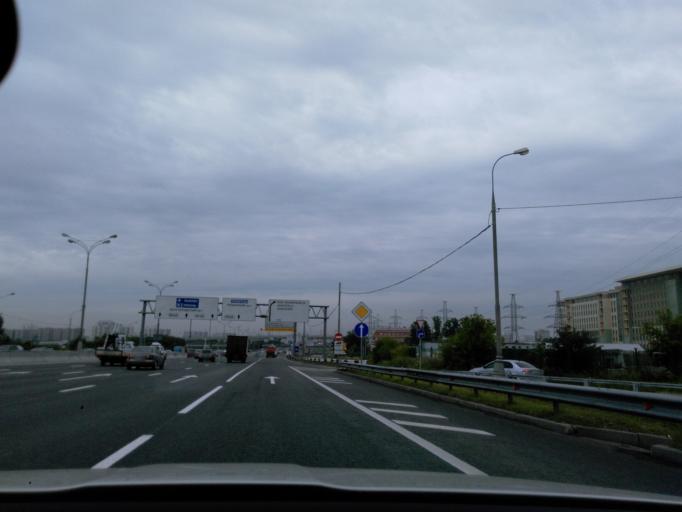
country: RU
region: Moscow
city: Veshnyaki
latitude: 55.7176
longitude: 37.8385
